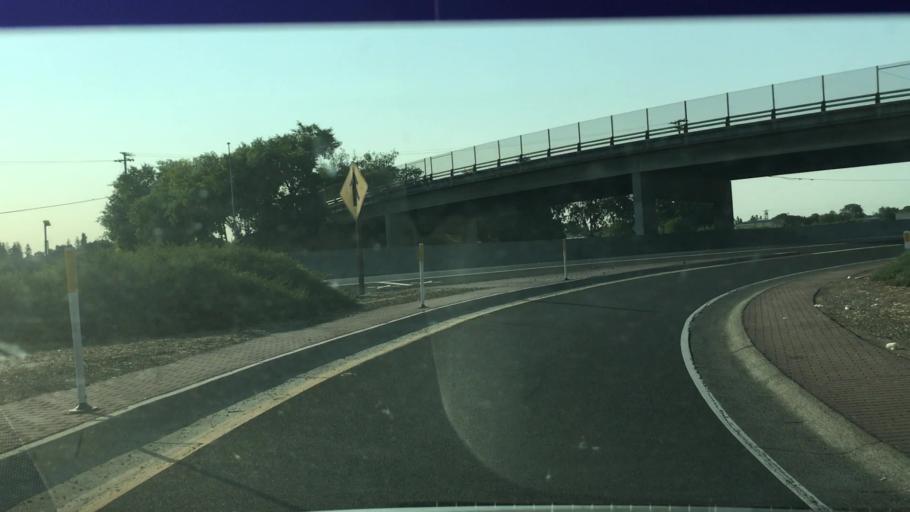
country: US
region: California
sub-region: San Joaquin County
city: Lodi
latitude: 38.0879
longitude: -121.2605
